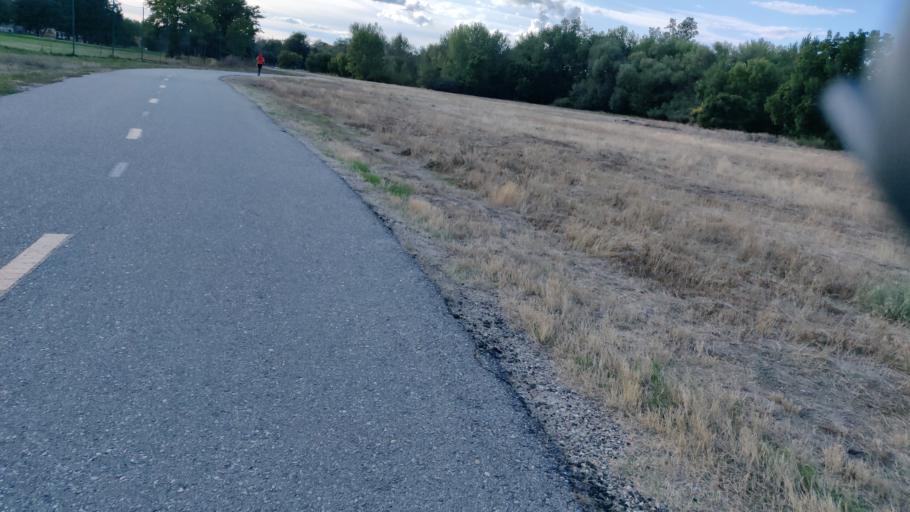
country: US
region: Idaho
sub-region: Ada County
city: Boise
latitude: 43.6005
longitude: -116.1711
